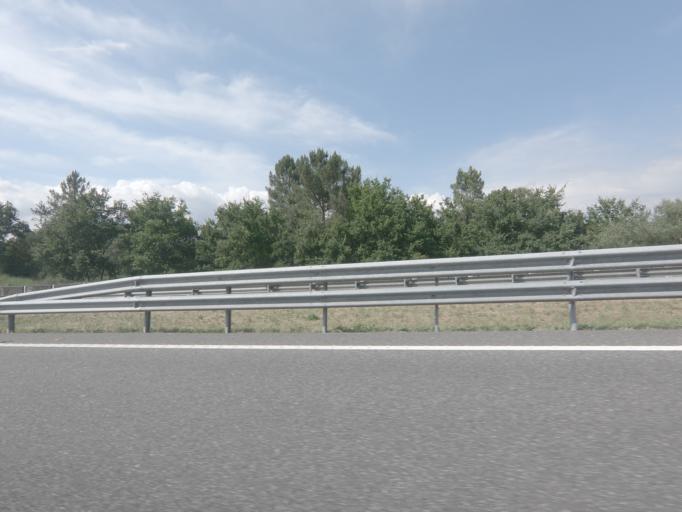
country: ES
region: Galicia
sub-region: Provincia de Ourense
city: Toen
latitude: 42.3326
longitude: -7.9641
